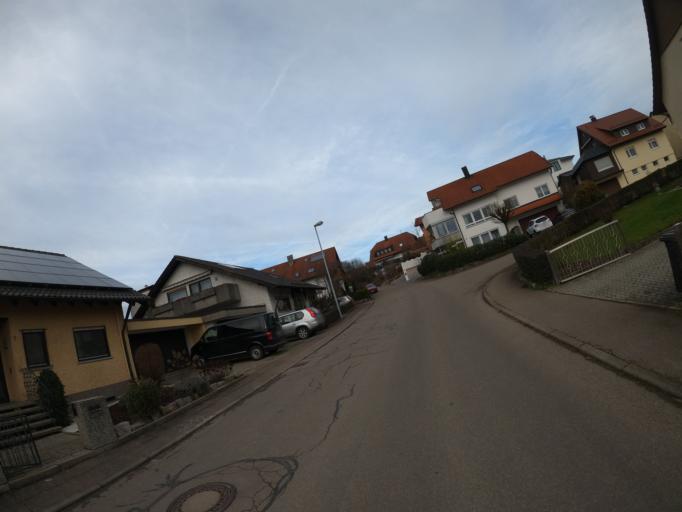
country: DE
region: Baden-Wuerttemberg
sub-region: Regierungsbezirk Stuttgart
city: Ottenbach
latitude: 48.7332
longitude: 9.7442
